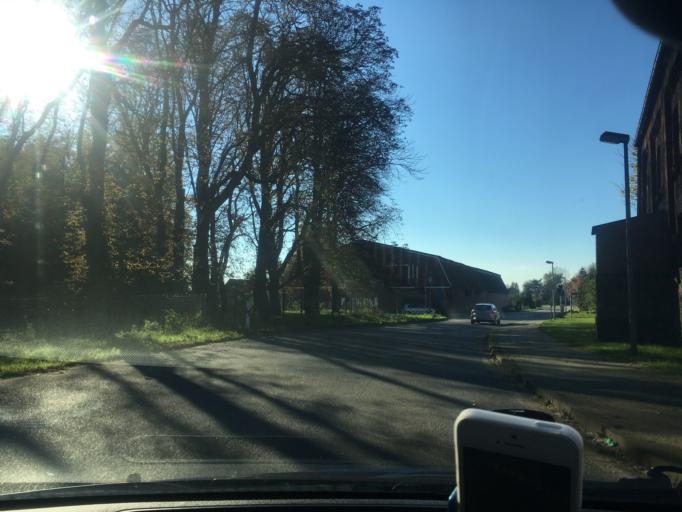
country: DE
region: Mecklenburg-Vorpommern
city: Wittenburg
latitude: 53.5341
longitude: 11.1170
